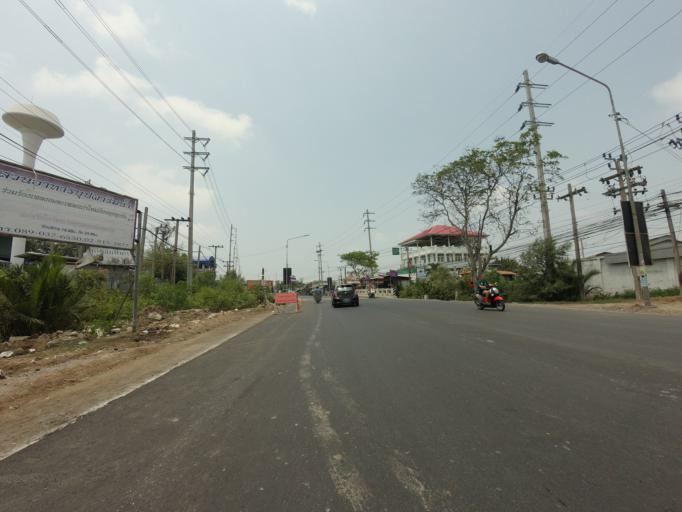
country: TH
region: Samut Prakan
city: Phra Samut Chedi
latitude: 13.5782
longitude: 100.5747
